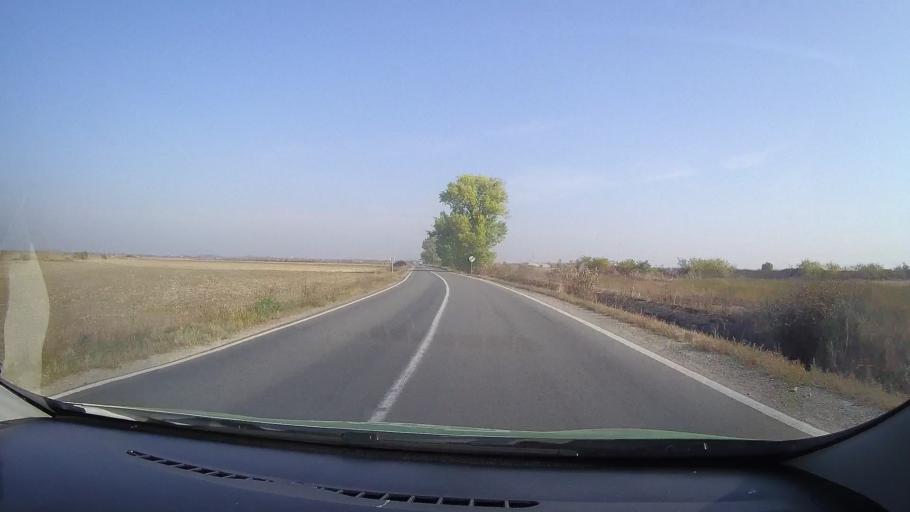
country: RO
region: Arad
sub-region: Comuna Pilu
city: Pilu
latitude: 46.5980
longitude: 21.3493
